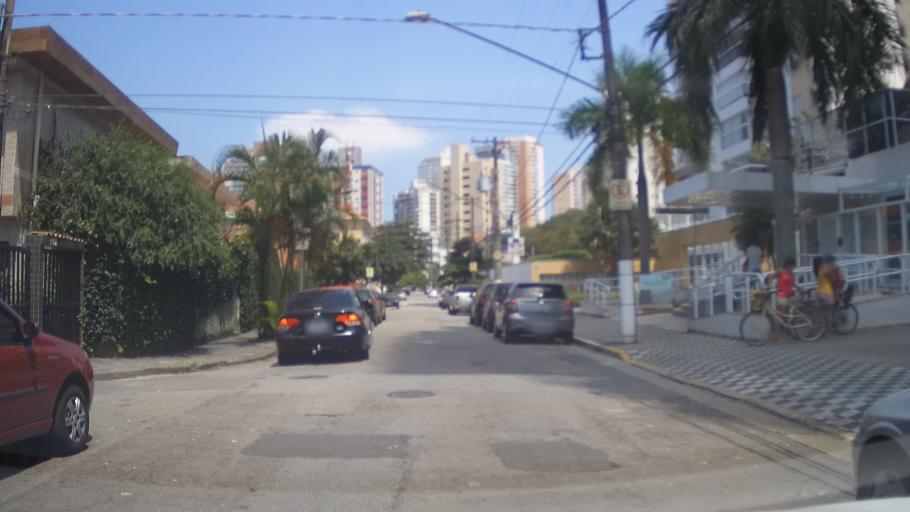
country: BR
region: Sao Paulo
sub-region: Guaruja
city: Guaruja
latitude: -23.9833
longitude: -46.2961
